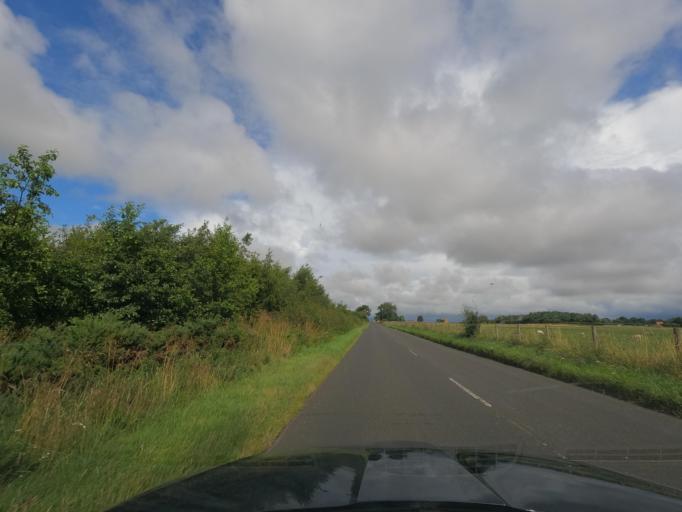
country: GB
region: England
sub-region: Northumberland
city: Lowick
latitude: 55.6381
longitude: -1.9919
